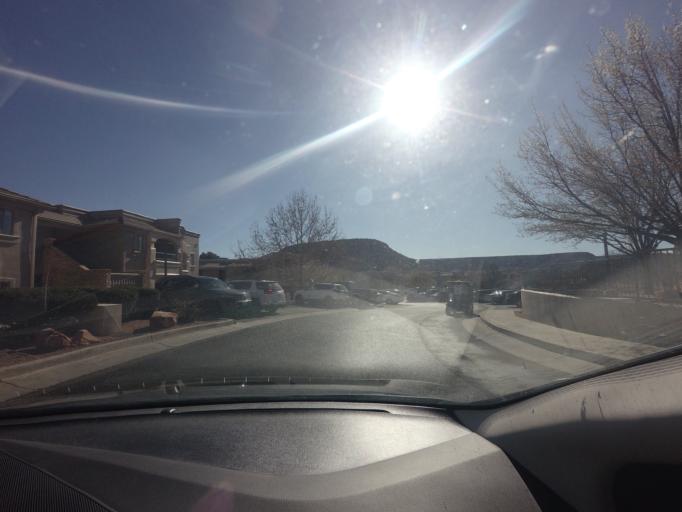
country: US
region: Arizona
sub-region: Yavapai County
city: Big Park
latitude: 34.7723
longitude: -111.7690
